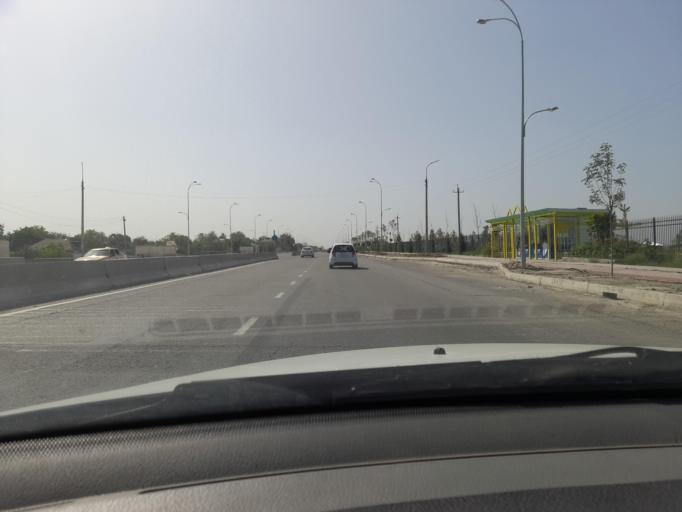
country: UZ
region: Samarqand
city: Samarqand
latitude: 39.7060
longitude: 66.9952
